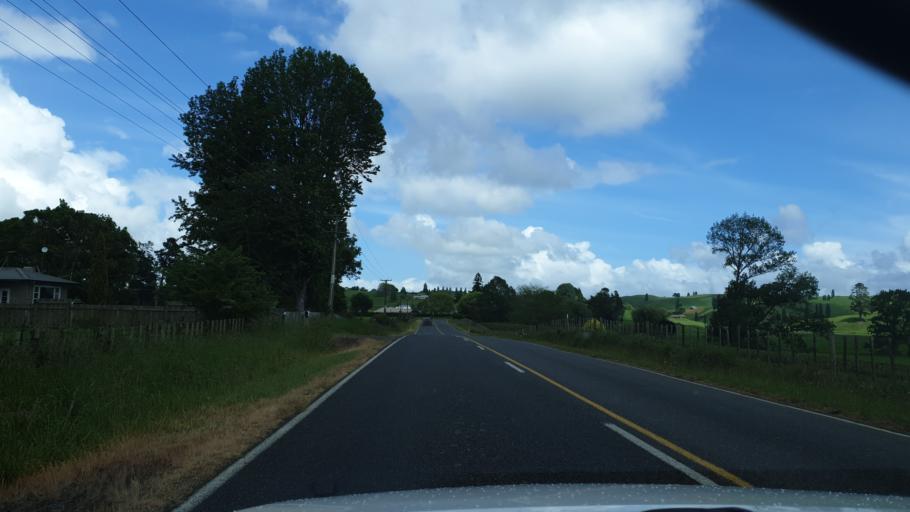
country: NZ
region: Waikato
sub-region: Matamata-Piako District
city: Matamata
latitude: -37.8781
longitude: 175.7127
